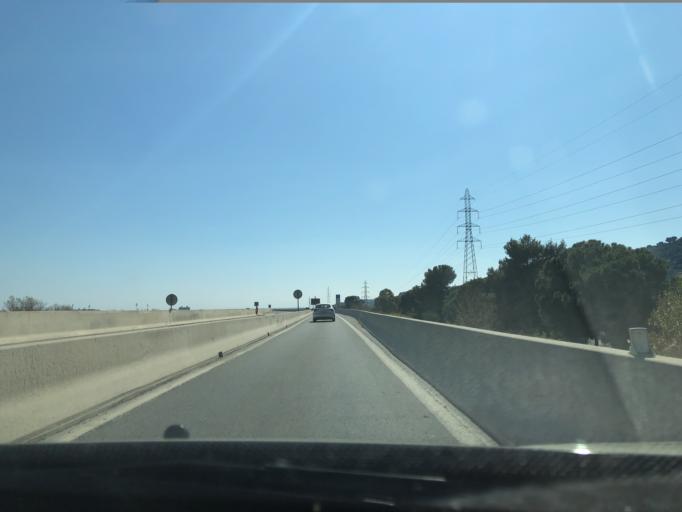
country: FR
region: Provence-Alpes-Cote d'Azur
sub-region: Departement des Alpes-Maritimes
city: Saint-Laurent-du-Var
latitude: 43.7013
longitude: 7.1851
